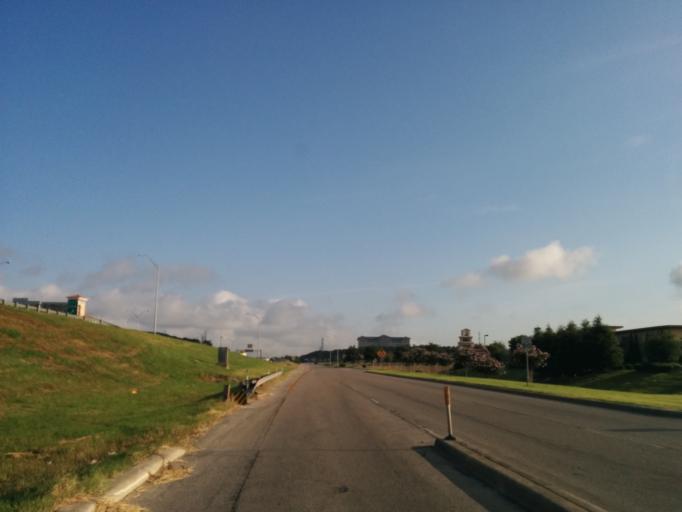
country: US
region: Texas
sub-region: Bexar County
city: Shavano Park
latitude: 29.6070
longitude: -98.6017
